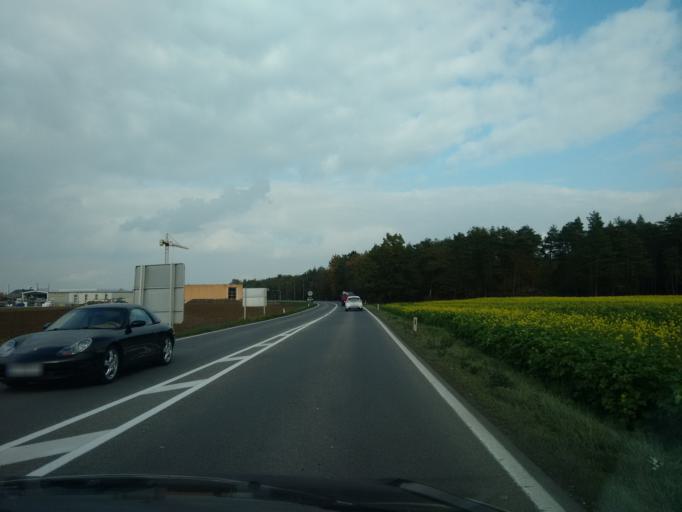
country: AT
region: Upper Austria
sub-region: Wels-Land
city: Gunskirchen
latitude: 48.1325
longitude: 13.9603
